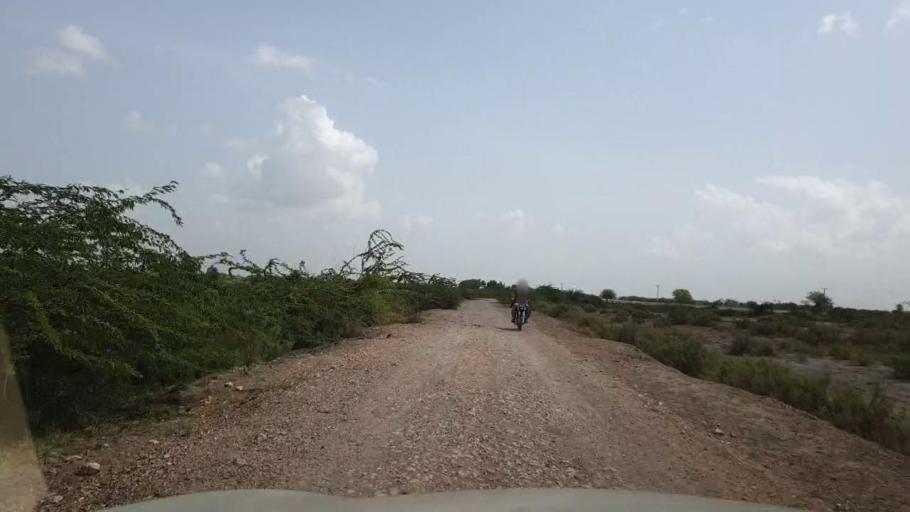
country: PK
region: Sindh
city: Kadhan
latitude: 24.3990
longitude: 68.7974
